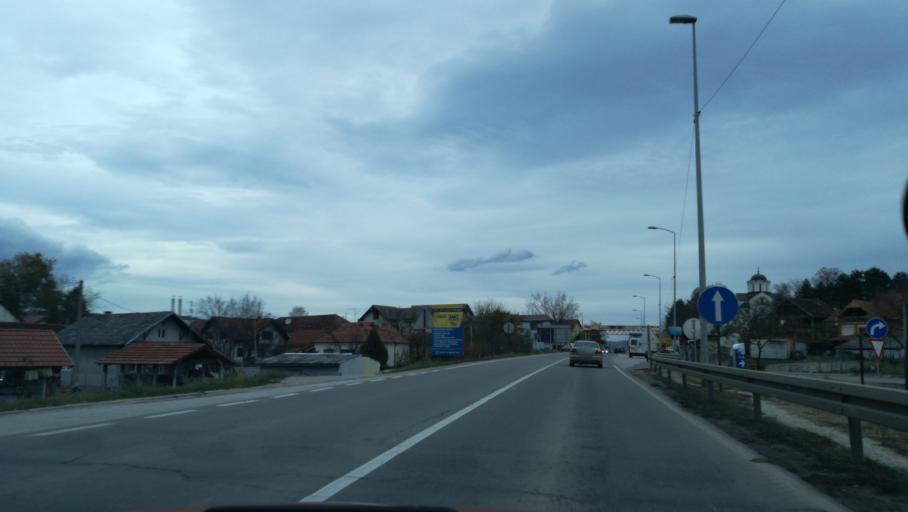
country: RS
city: Prislonica
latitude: 43.9140
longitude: 20.4076
